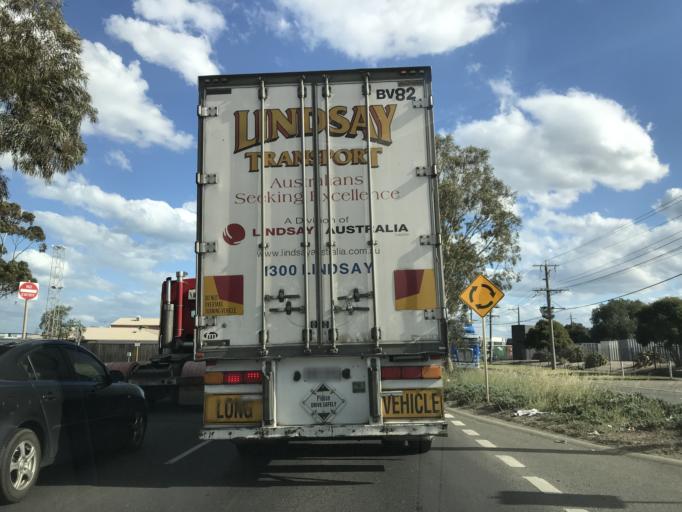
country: AU
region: Victoria
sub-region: Brimbank
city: Sunshine West
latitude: -37.8151
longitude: 144.8170
